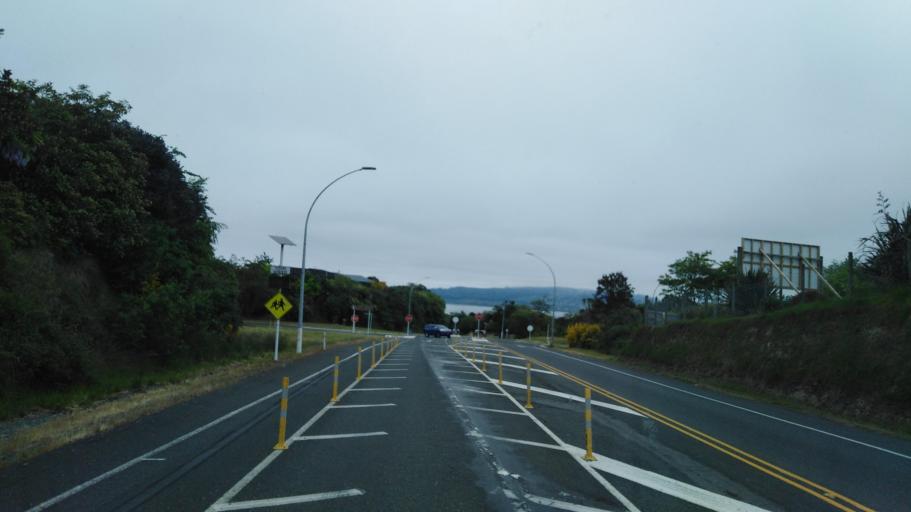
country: NZ
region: Waikato
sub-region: Taupo District
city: Taupo
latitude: -38.7041
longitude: 176.0975
